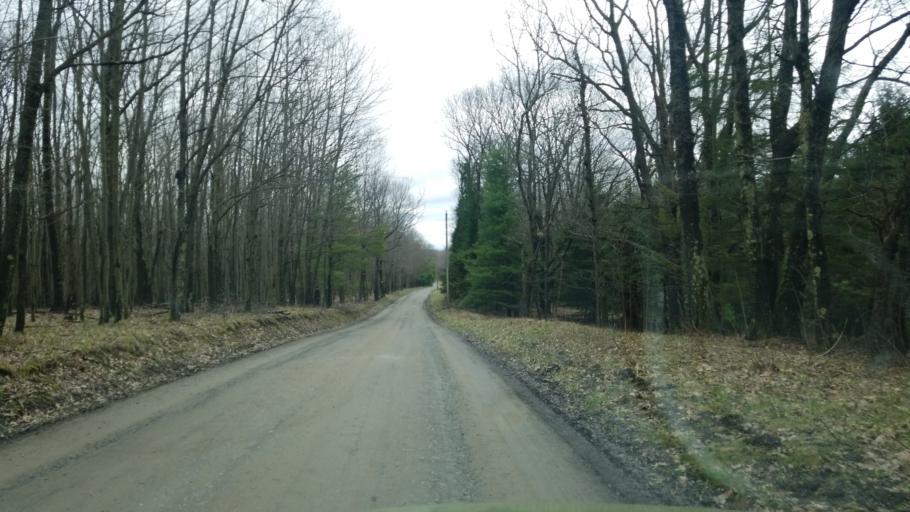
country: US
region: Pennsylvania
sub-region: Clearfield County
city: Shiloh
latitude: 41.1802
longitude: -78.3344
